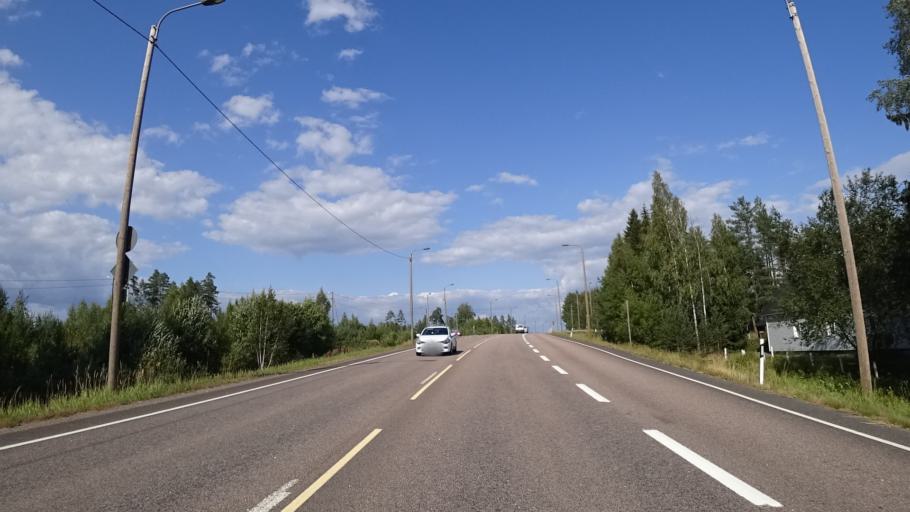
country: FI
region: Kymenlaakso
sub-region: Kotka-Hamina
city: Hamina
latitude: 60.6140
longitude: 27.1907
